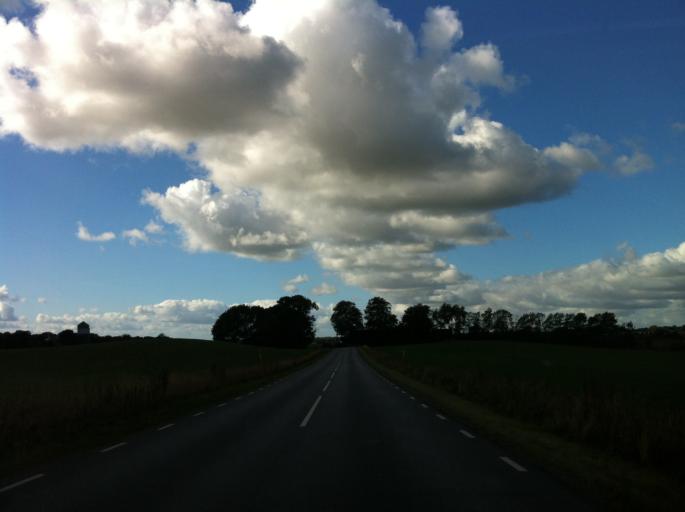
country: SE
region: Skane
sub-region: Tomelilla Kommun
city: Tomelilla
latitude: 55.6437
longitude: 13.9891
